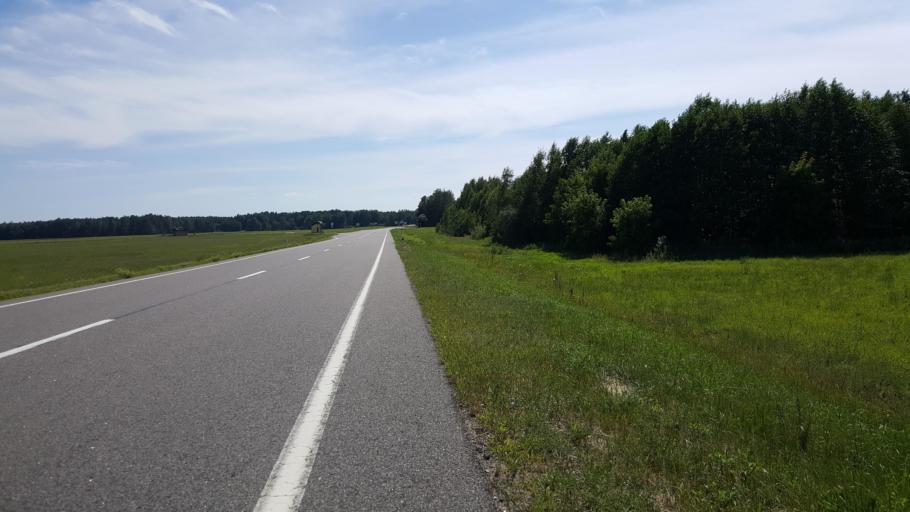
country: BY
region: Brest
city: Zhabinka
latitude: 52.4621
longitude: 24.1429
